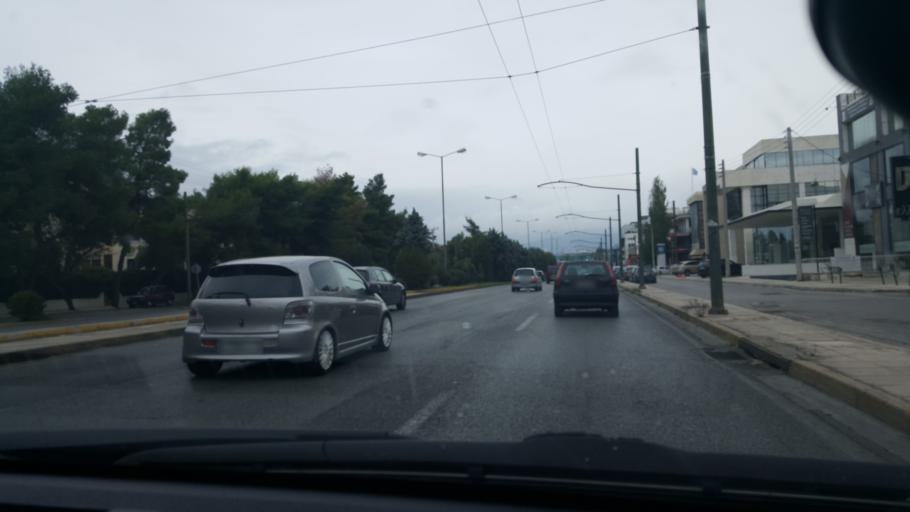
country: GR
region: Attica
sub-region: Nomarchia Athinas
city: Neo Psychiko
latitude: 38.0131
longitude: 23.7830
